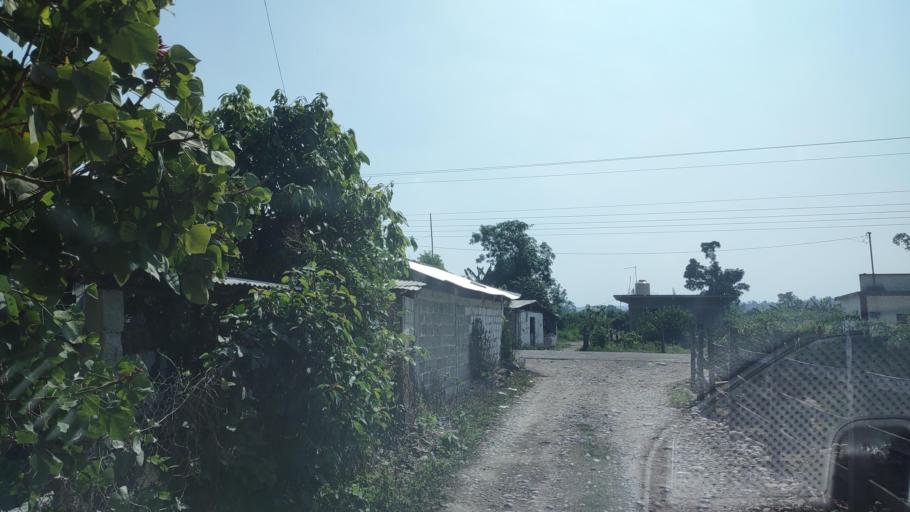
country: MX
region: Puebla
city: Espinal
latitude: 20.2516
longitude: -97.3378
